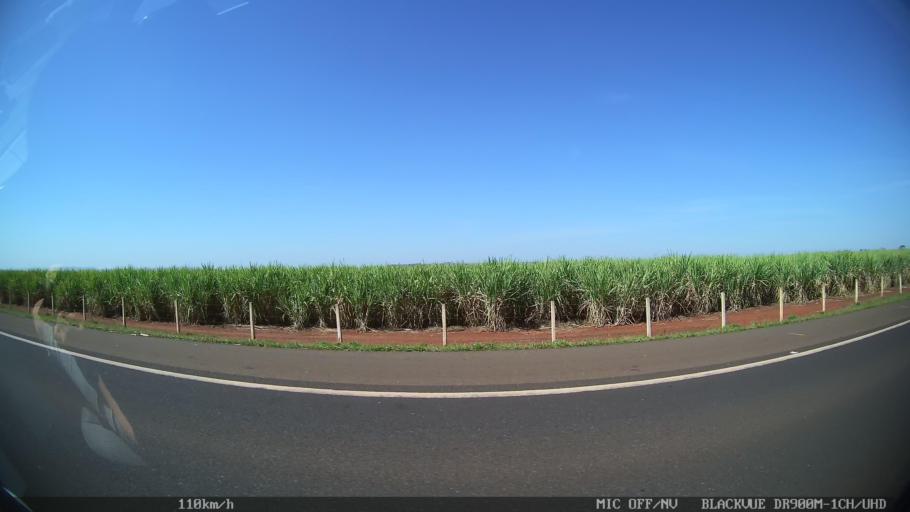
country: BR
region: Sao Paulo
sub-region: Batatais
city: Batatais
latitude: -20.7796
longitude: -47.5490
